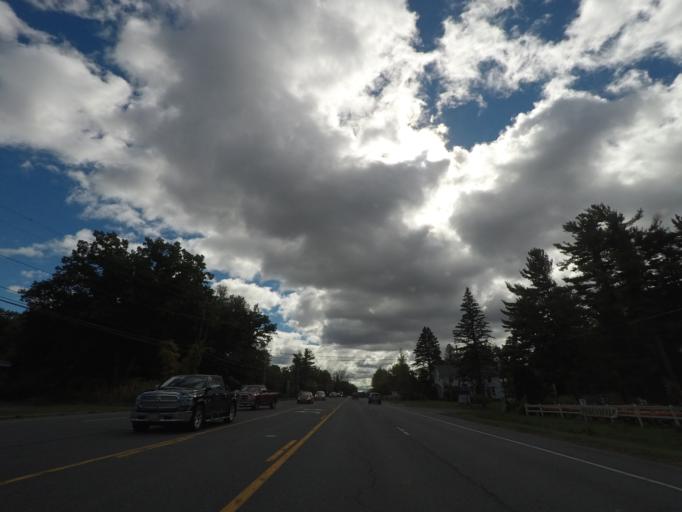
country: US
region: New York
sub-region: Saratoga County
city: Waterford
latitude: 42.8343
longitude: -73.7392
